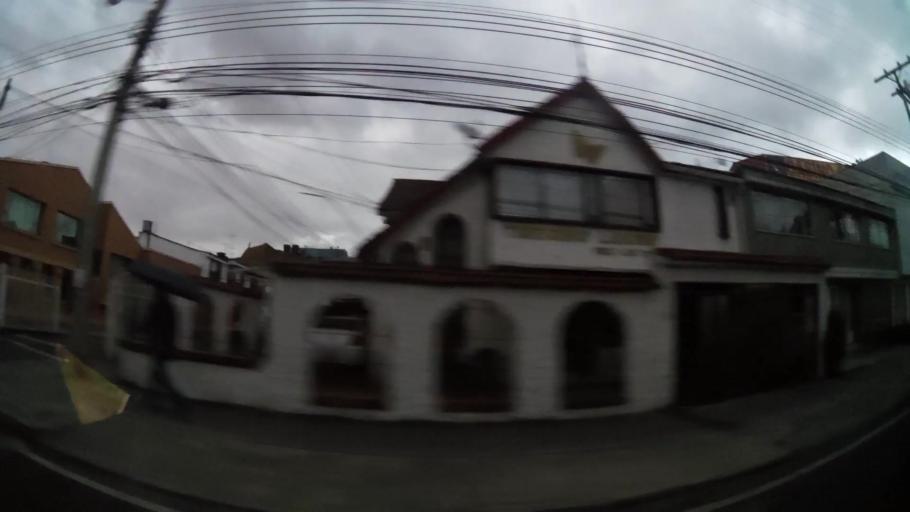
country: CO
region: Bogota D.C.
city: Bogota
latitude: 4.6719
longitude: -74.1080
